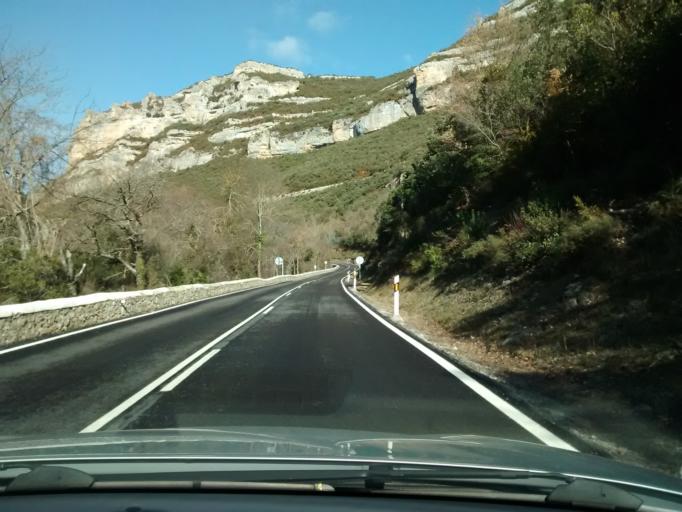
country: ES
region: Castille and Leon
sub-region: Provincia de Burgos
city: Medina de Pomar
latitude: 42.8646
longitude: -3.5923
